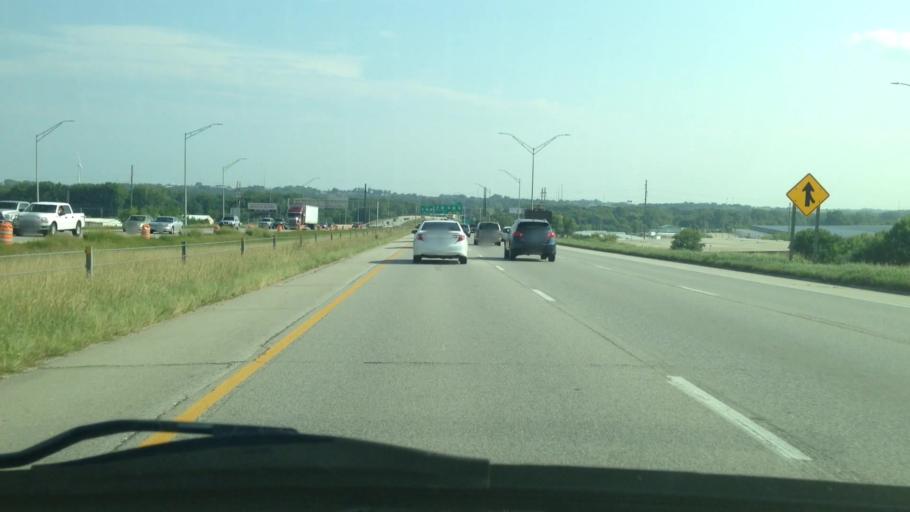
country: US
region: Iowa
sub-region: Linn County
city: Cedar Rapids
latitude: 41.9443
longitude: -91.6705
